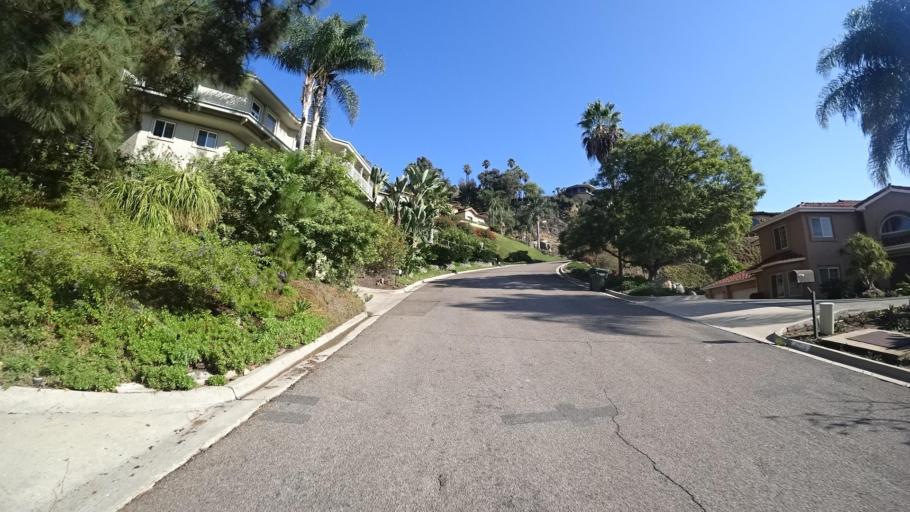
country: US
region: California
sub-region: San Diego County
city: Casa de Oro-Mount Helix
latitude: 32.7643
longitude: -116.9815
